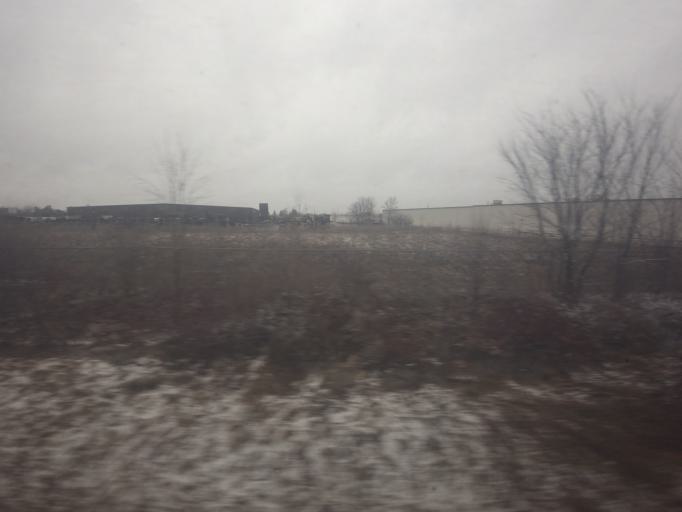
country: CA
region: Ontario
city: Brockville
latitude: 44.6102
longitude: -75.6954
